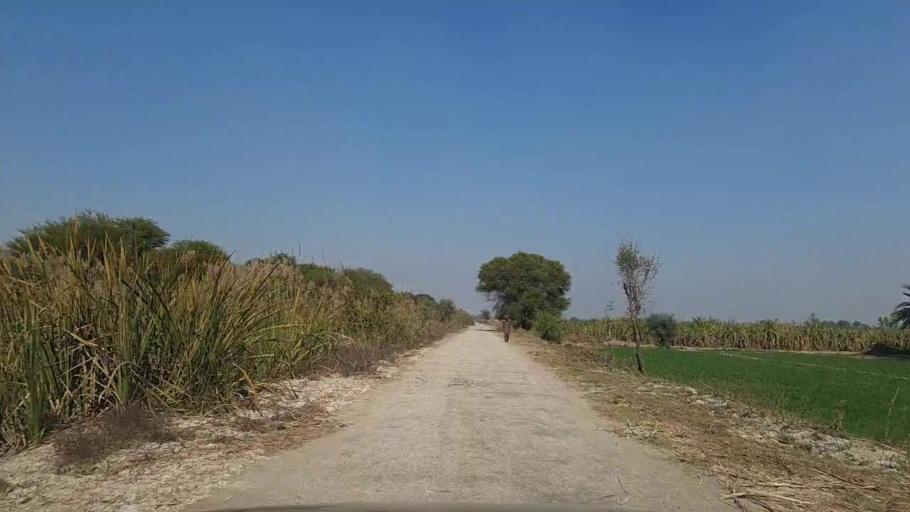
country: PK
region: Sindh
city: Daur
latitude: 26.5019
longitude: 68.3463
